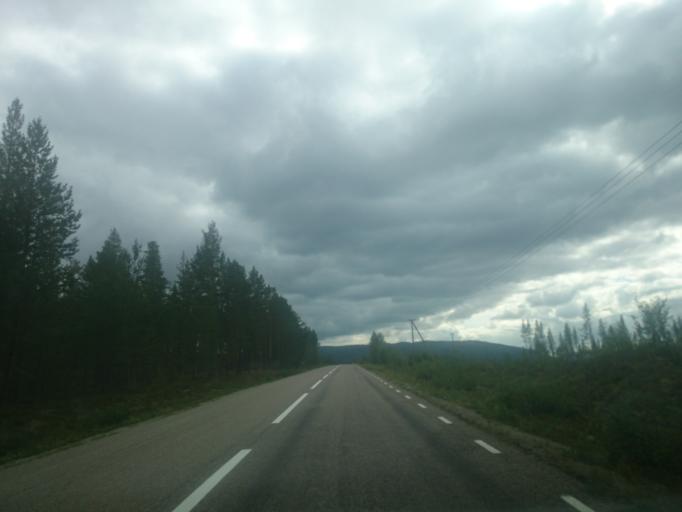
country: SE
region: Jaemtland
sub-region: Harjedalens Kommun
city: Sveg
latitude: 62.3818
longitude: 13.7714
